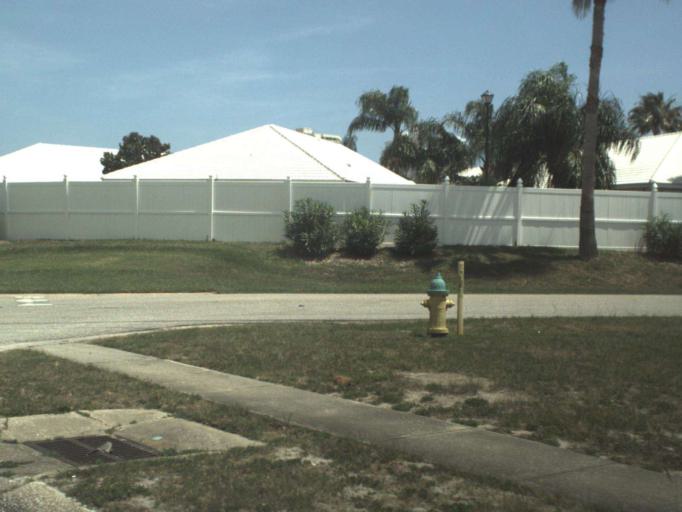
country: US
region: Florida
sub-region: Volusia County
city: Daytona Beach Shores
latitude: 29.1797
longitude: -80.9883
